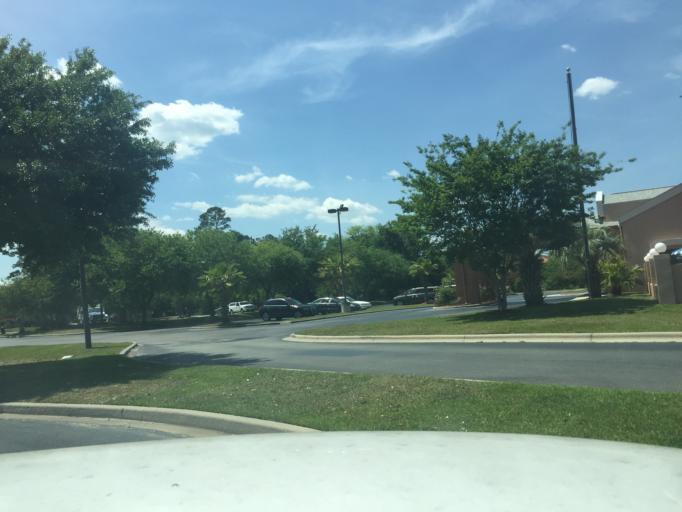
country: US
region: Georgia
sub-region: Chatham County
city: Georgetown
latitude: 32.0048
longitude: -81.2763
